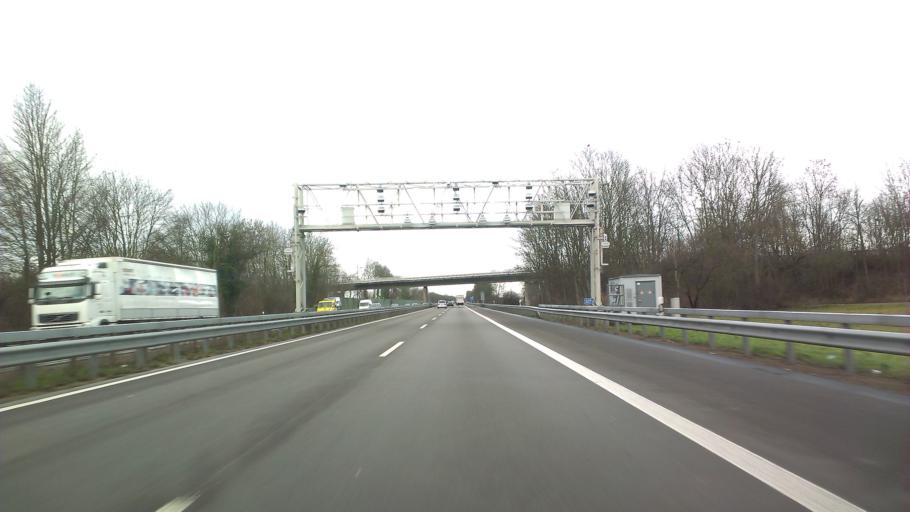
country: DE
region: Rheinland-Pfalz
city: Dintesheim
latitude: 49.7071
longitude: 8.1517
